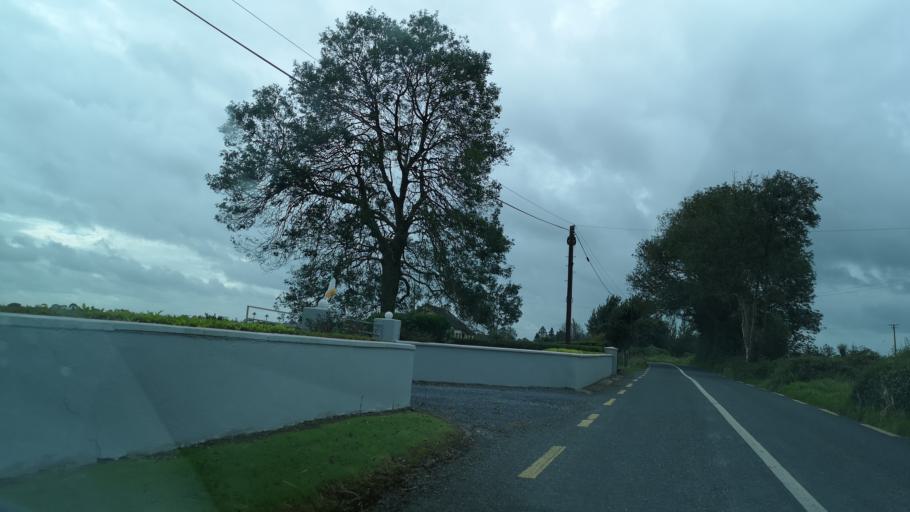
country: IE
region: Connaught
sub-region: County Galway
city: Loughrea
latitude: 53.2831
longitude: -8.6150
